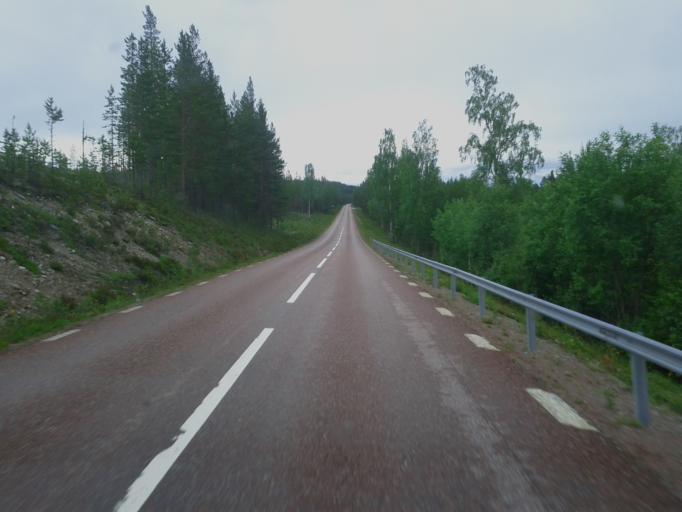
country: NO
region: Hedmark
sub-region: Trysil
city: Innbygda
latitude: 61.8067
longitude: 12.9070
